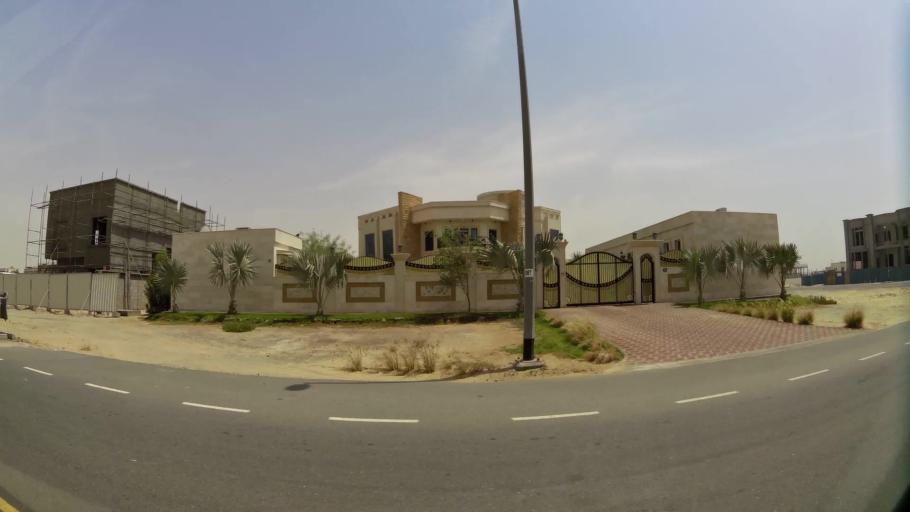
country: AE
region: Ash Shariqah
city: Sharjah
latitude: 25.2497
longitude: 55.5050
